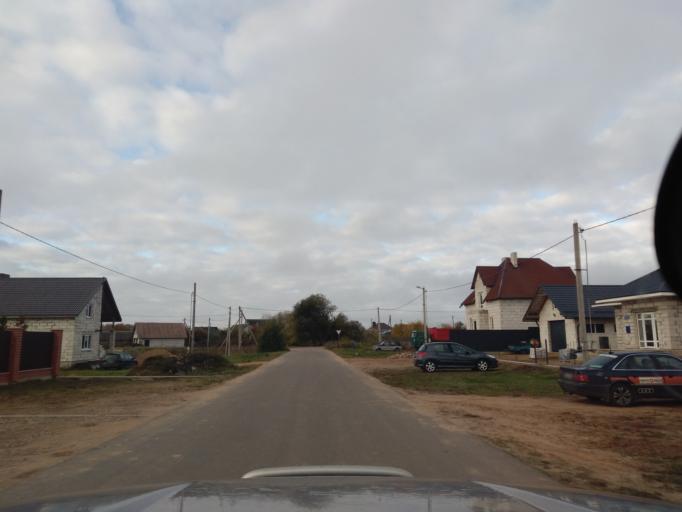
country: BY
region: Minsk
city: Kapyl'
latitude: 53.1605
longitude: 27.1003
